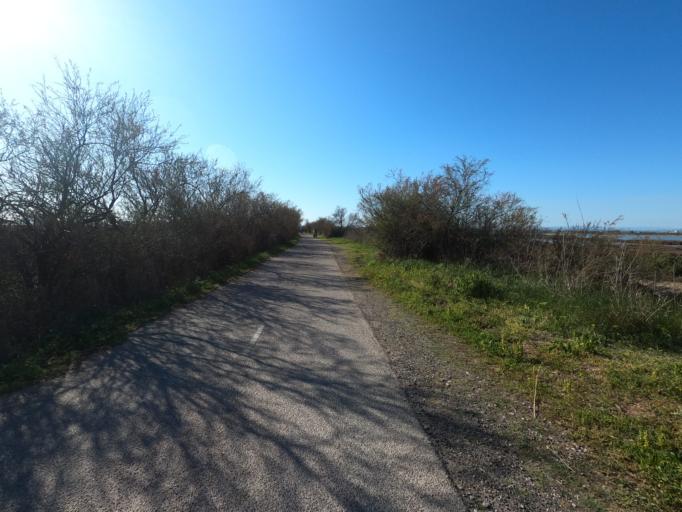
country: FR
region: Languedoc-Roussillon
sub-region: Departement de l'Herault
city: Palavas-les-Flots
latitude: 43.5357
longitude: 3.9158
